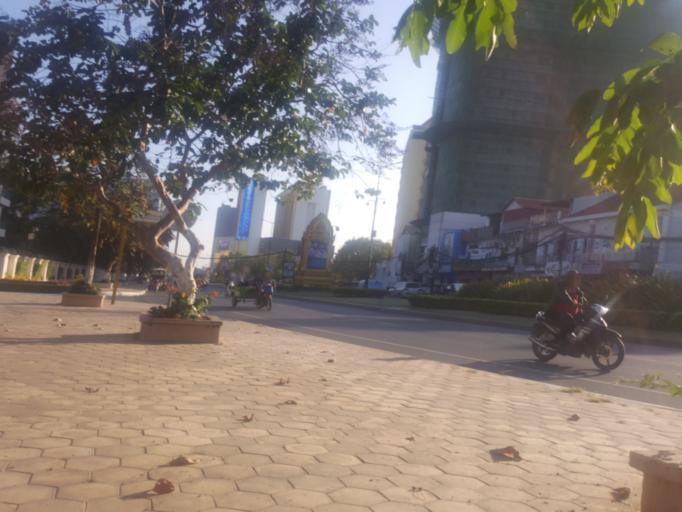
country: KH
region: Phnom Penh
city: Phnom Penh
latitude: 11.5615
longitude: 104.9354
